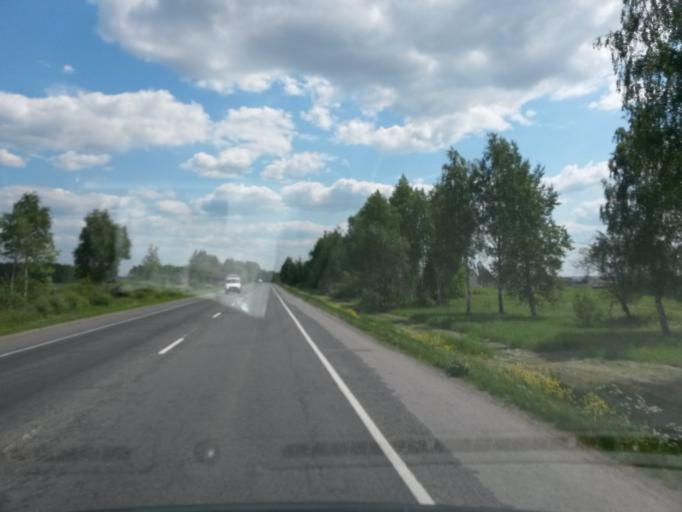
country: RU
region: Jaroslavl
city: Yaroslavl
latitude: 57.5568
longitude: 39.8670
